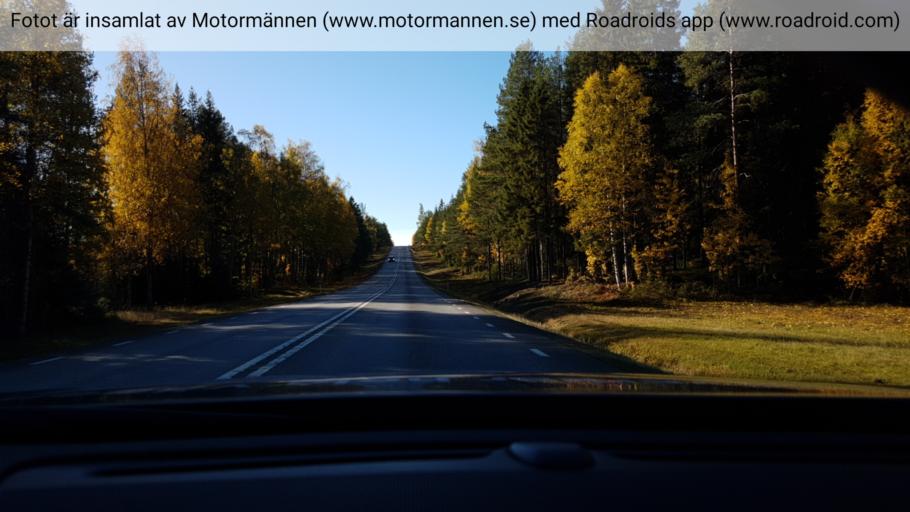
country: SE
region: Vaesterbotten
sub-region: Robertsfors Kommun
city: Robertsfors
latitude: 64.2006
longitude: 21.0123
